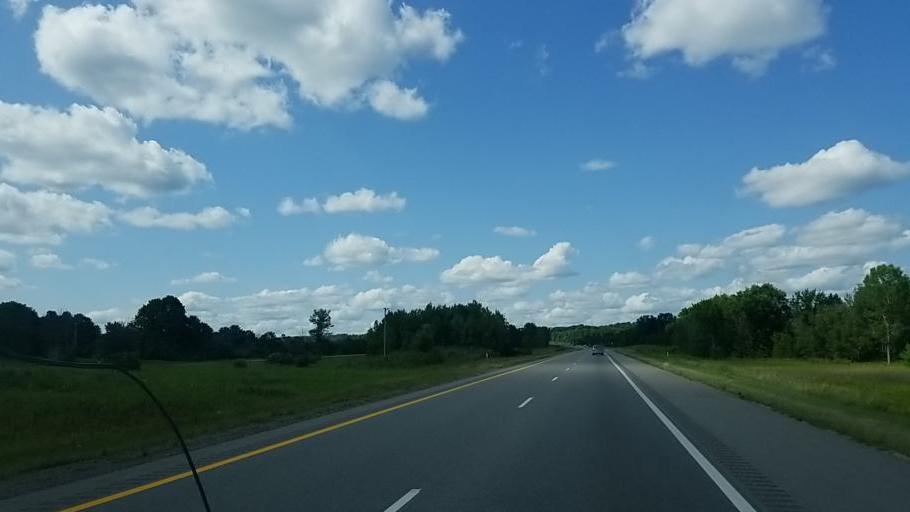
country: US
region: Michigan
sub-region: Mecosta County
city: Big Rapids
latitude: 43.6185
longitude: -85.4973
